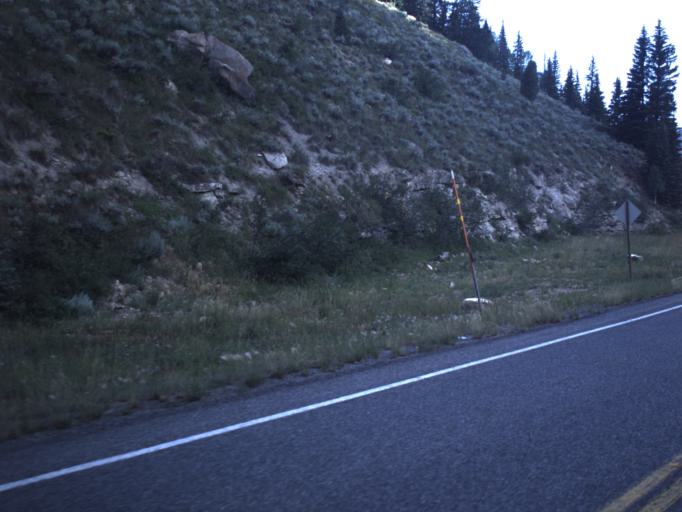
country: US
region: Utah
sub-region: Emery County
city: Huntington
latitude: 39.5047
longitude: -111.1565
